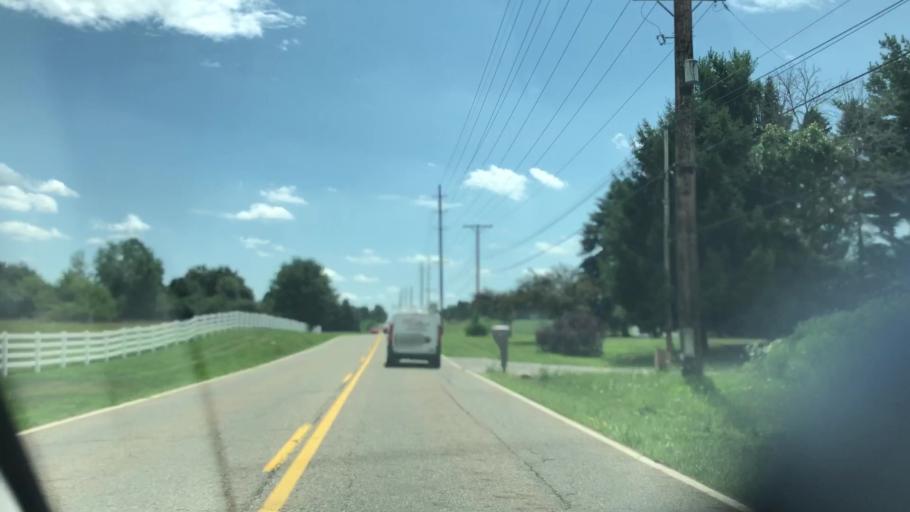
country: US
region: Ohio
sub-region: Summit County
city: Greensburg
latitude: 40.8828
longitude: -81.4993
